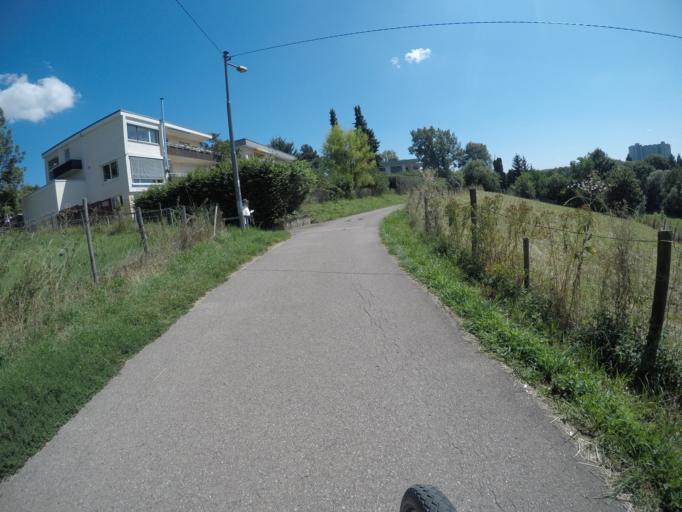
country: DE
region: Baden-Wuerttemberg
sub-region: Regierungsbezirk Stuttgart
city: Leinfelden-Echterdingen
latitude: 48.7210
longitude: 9.1558
